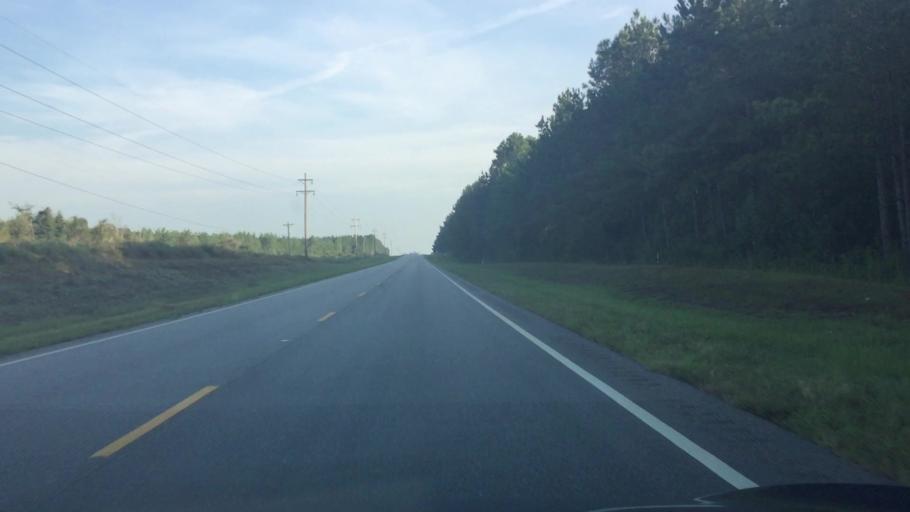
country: US
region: Alabama
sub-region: Covington County
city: Florala
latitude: 31.0375
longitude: -86.3774
